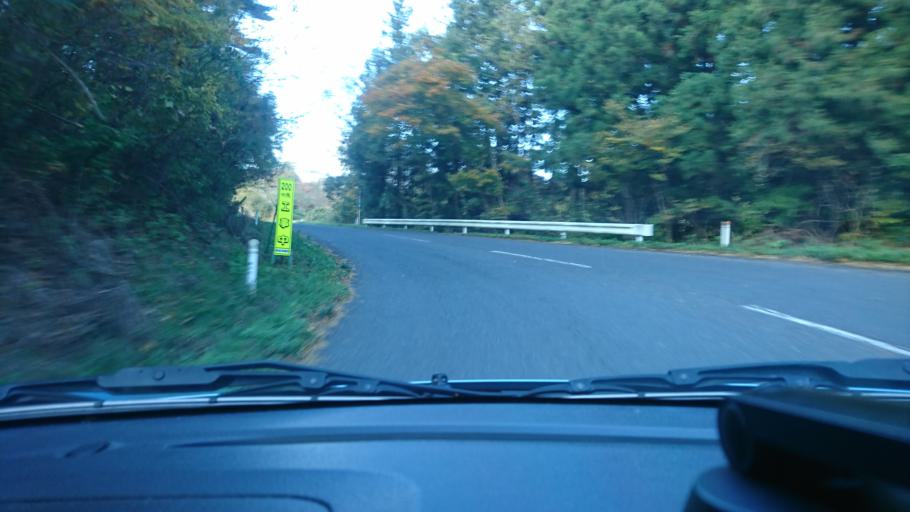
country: JP
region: Iwate
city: Ichinoseki
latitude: 38.7987
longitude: 141.2565
